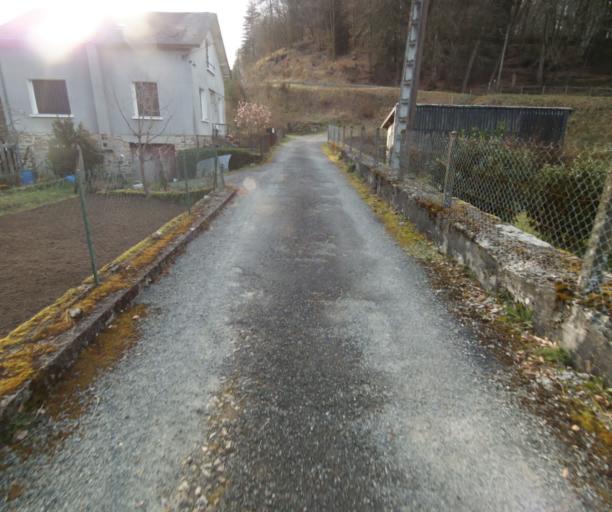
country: FR
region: Limousin
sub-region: Departement de la Correze
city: Correze
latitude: 45.3730
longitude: 1.8811
